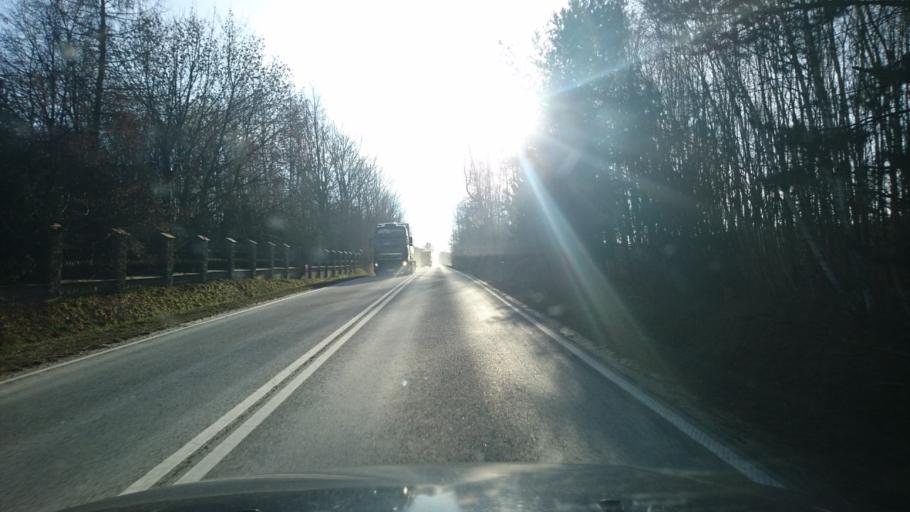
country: PL
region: Opole Voivodeship
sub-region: Powiat oleski
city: Dalachow
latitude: 51.0734
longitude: 18.6022
